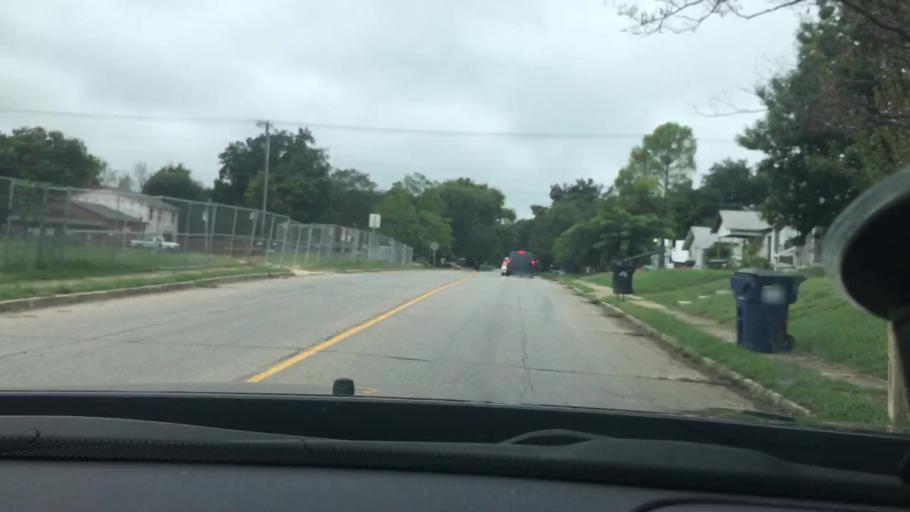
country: US
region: Oklahoma
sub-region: Pontotoc County
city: Ada
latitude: 34.7819
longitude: -96.6857
